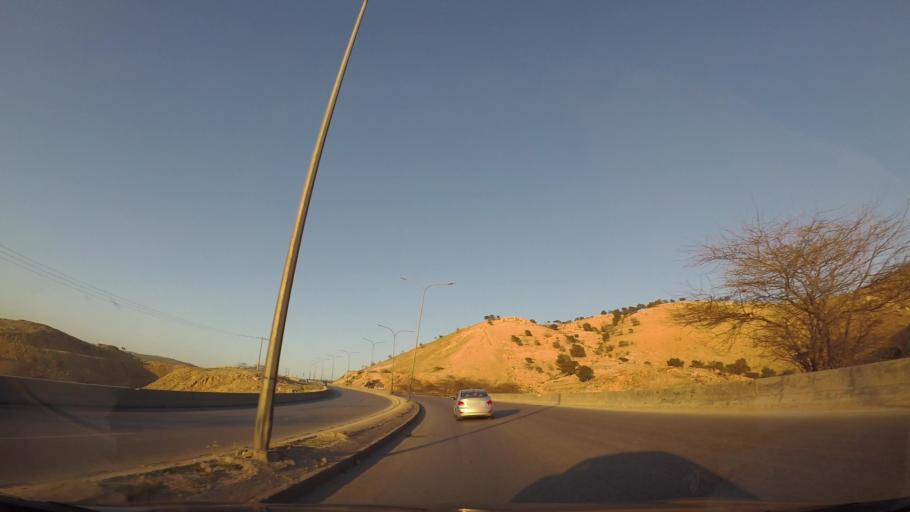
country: JO
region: Balqa
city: Yarqa
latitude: 31.8670
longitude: 35.7298
